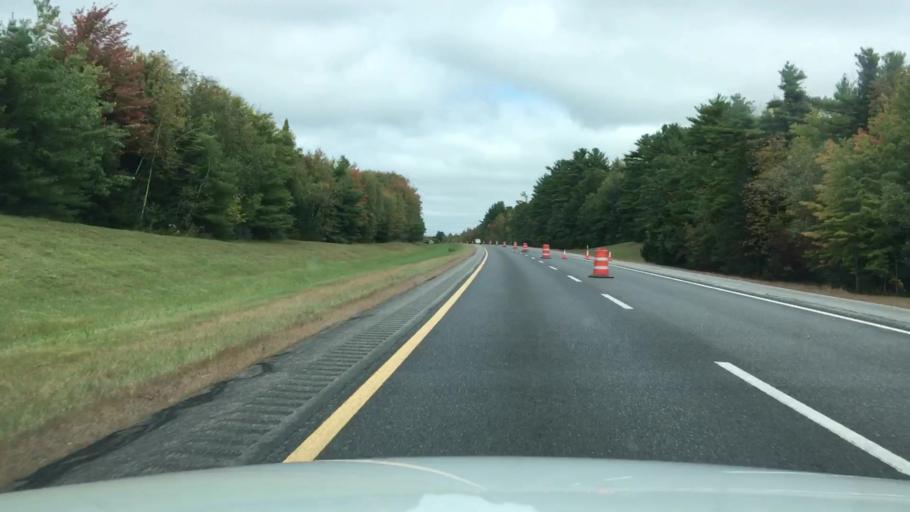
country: US
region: Maine
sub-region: Sagadahoc County
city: Richmond
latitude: 44.1217
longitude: -69.8505
